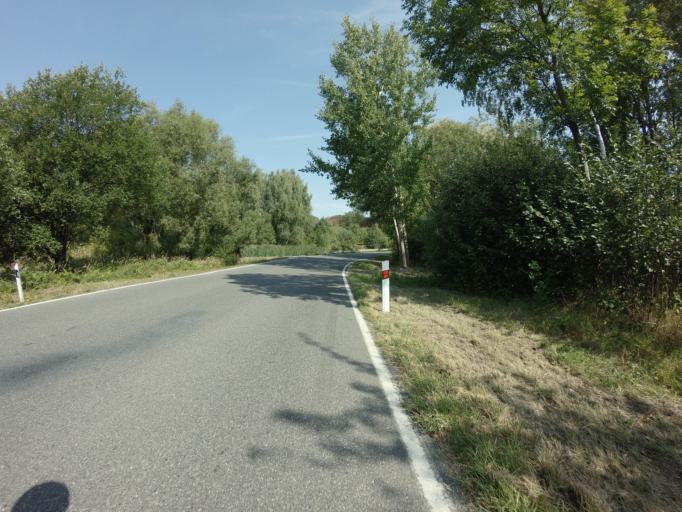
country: CZ
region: Central Bohemia
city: Sedlcany
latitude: 49.6112
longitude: 14.3848
